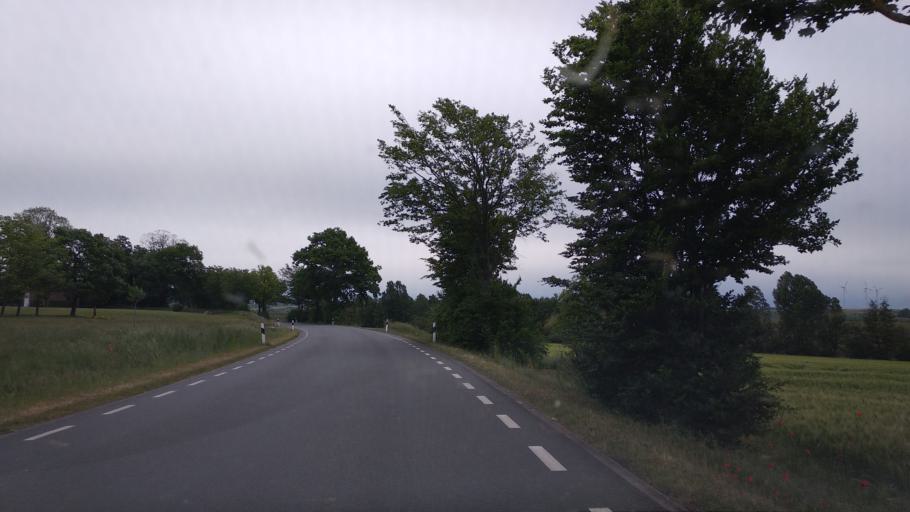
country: DE
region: North Rhine-Westphalia
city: Borgentreich
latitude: 51.5416
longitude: 9.2397
